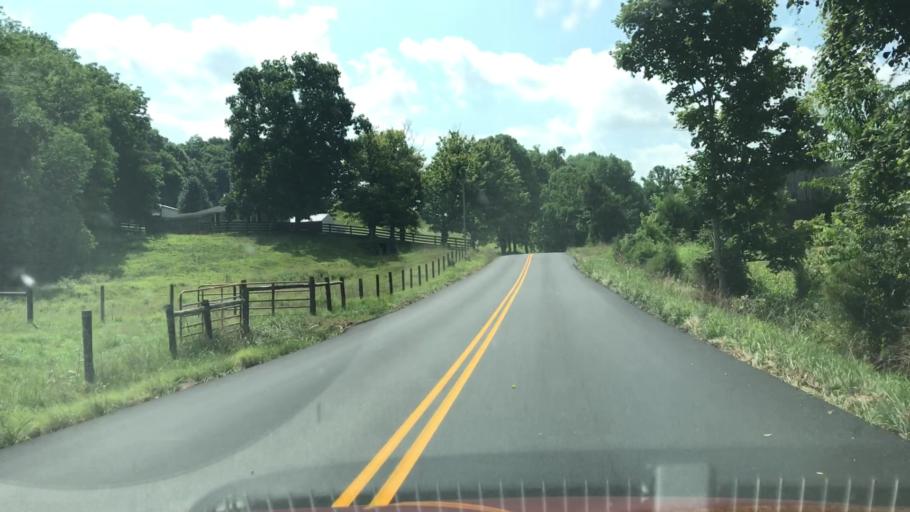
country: US
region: Kentucky
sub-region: Monroe County
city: Tompkinsville
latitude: 36.7616
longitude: -85.7941
